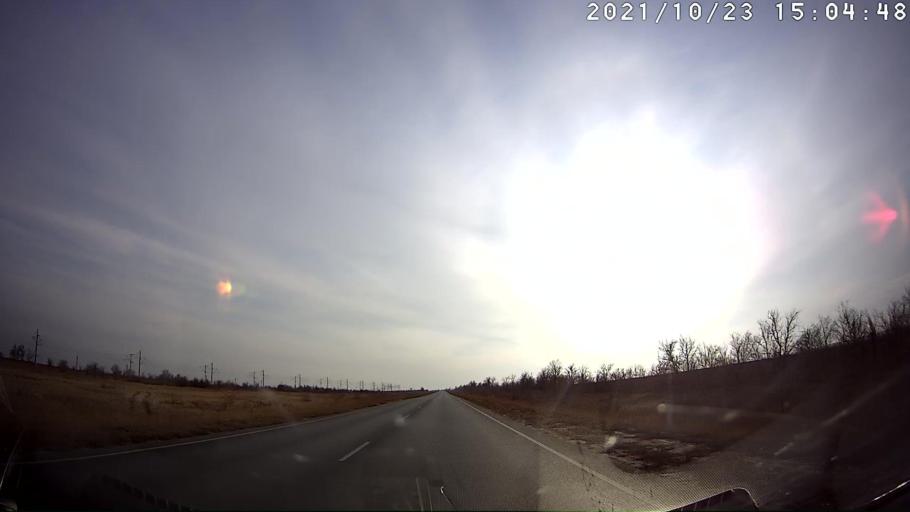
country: RU
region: Volgograd
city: Volgograd
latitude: 48.3938
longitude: 44.3648
